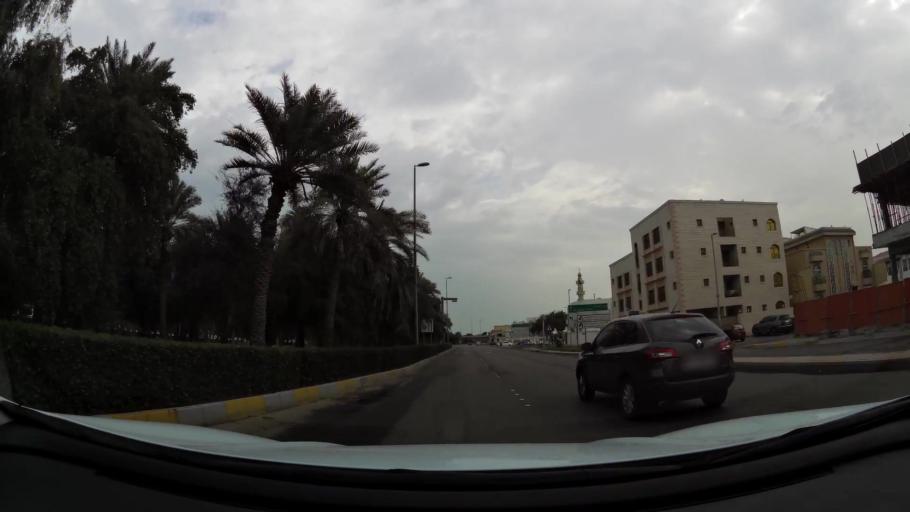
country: AE
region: Abu Dhabi
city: Abu Dhabi
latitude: 24.4518
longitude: 54.3990
